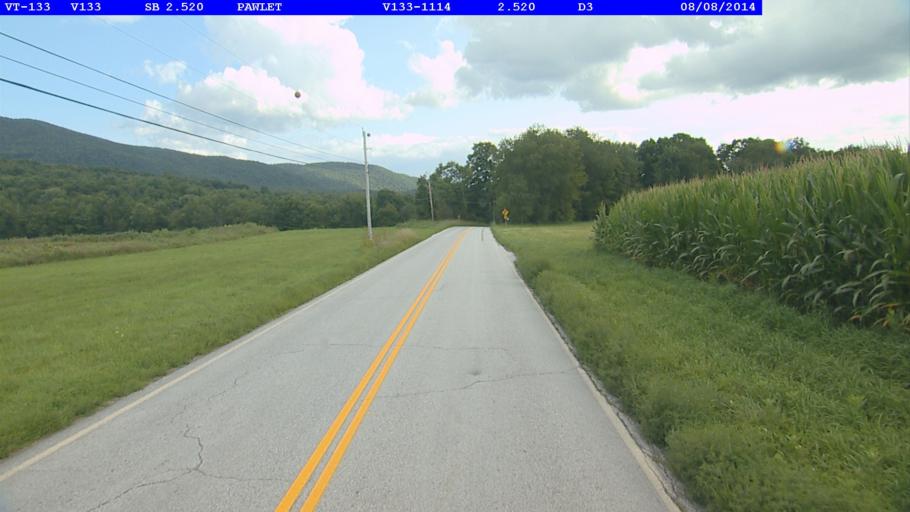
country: US
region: New York
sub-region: Washington County
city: Granville
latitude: 43.3677
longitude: -73.1454
